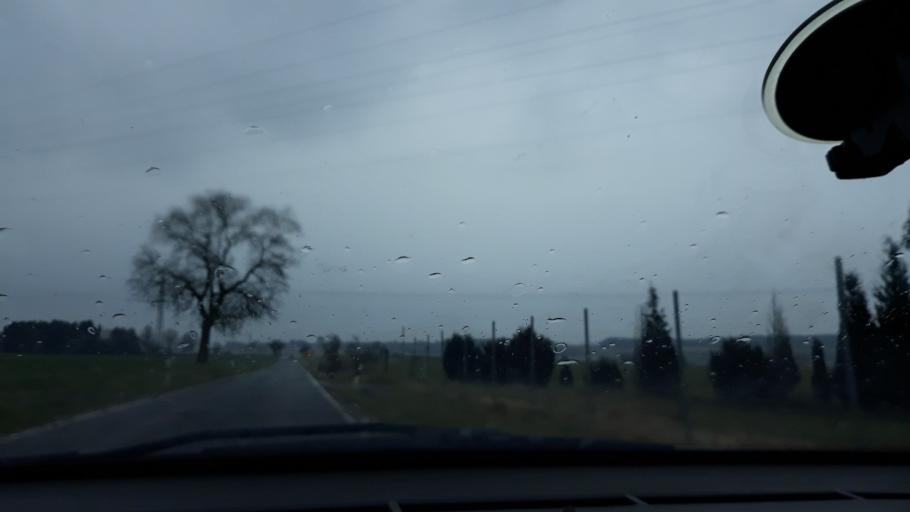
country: DE
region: Saarland
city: Gersheim
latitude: 49.2065
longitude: 7.1719
